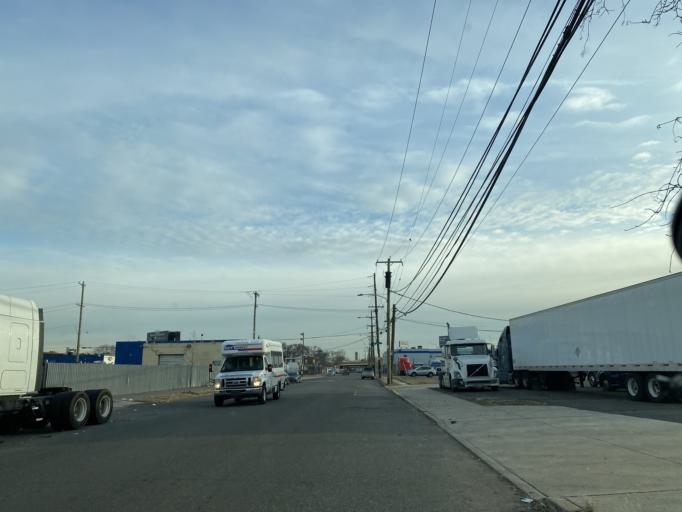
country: US
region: New Jersey
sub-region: Camden County
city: Pennsauken
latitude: 39.9955
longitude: -75.0878
